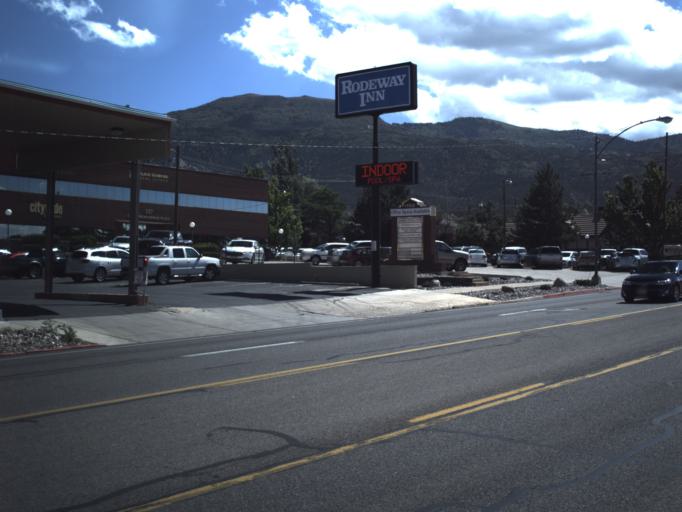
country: US
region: Utah
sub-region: Iron County
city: Cedar City
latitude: 37.6718
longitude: -113.0617
